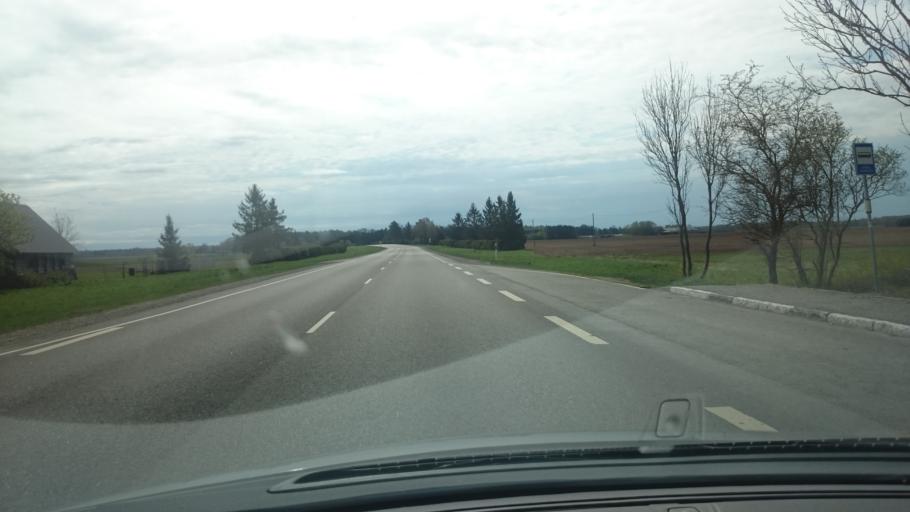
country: EE
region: Laeaene-Virumaa
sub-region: Rakvere linn
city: Rakvere
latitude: 59.4029
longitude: 26.3678
